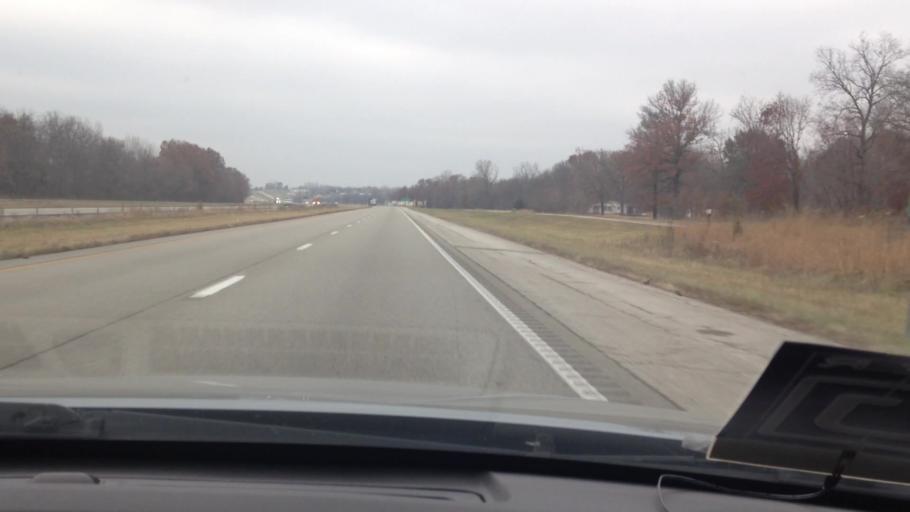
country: US
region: Missouri
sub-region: Cass County
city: Peculiar
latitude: 38.6937
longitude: -94.4287
